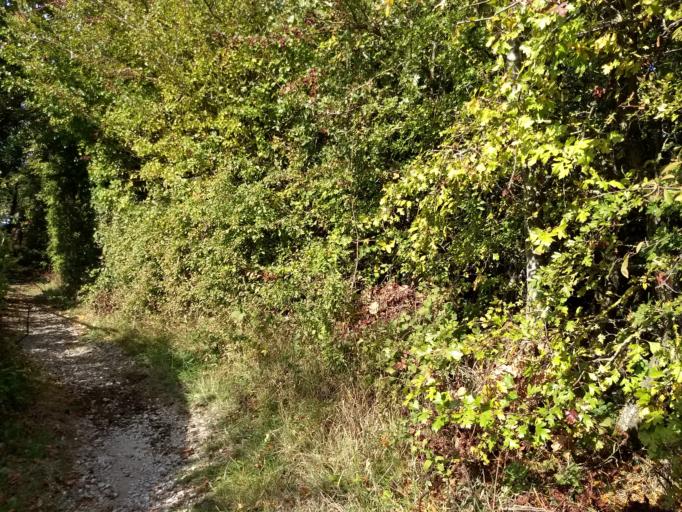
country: GB
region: England
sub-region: Isle of Wight
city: Seaview
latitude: 50.7071
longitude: -1.1190
